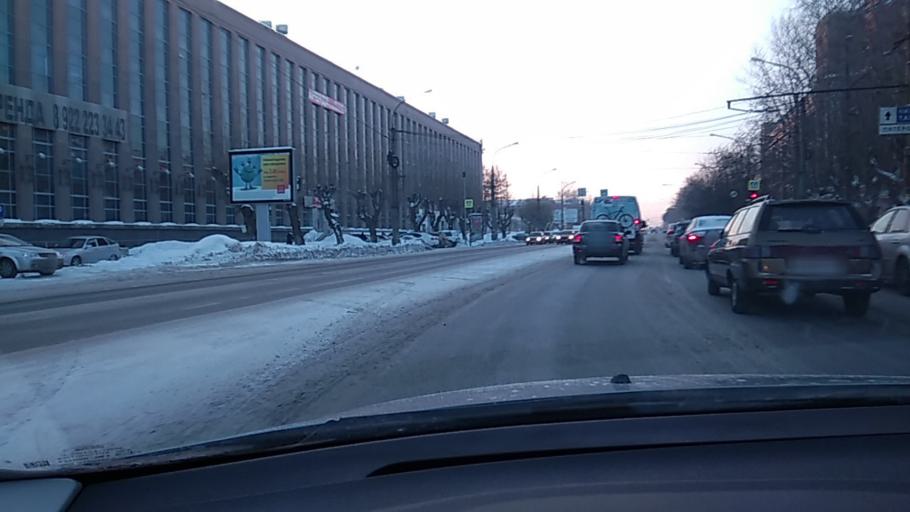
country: RU
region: Sverdlovsk
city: Yekaterinburg
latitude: 56.8858
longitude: 60.5903
